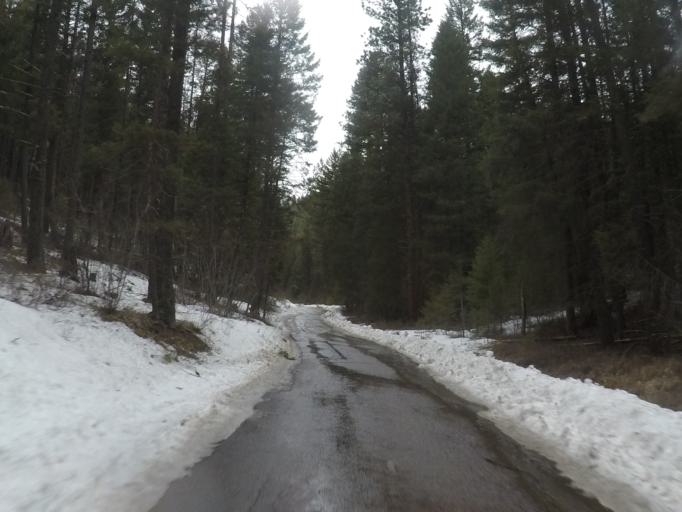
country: US
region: Montana
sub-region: Missoula County
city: East Missoula
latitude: 46.9279
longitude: -113.9664
